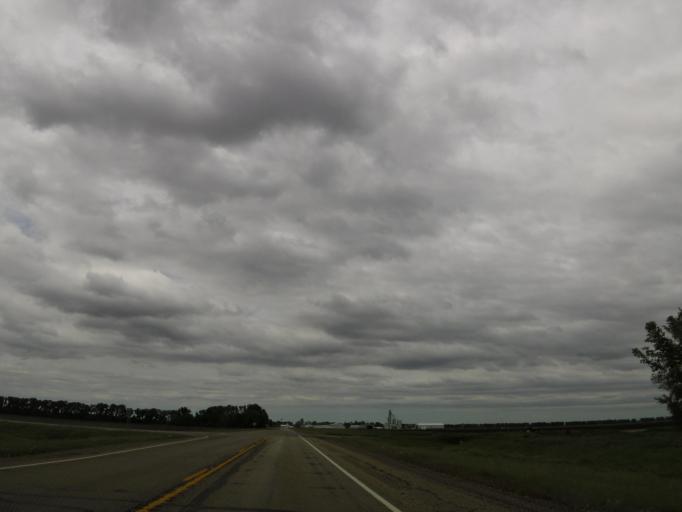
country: US
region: North Dakota
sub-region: Walsh County
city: Grafton
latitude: 48.6002
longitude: -97.4475
